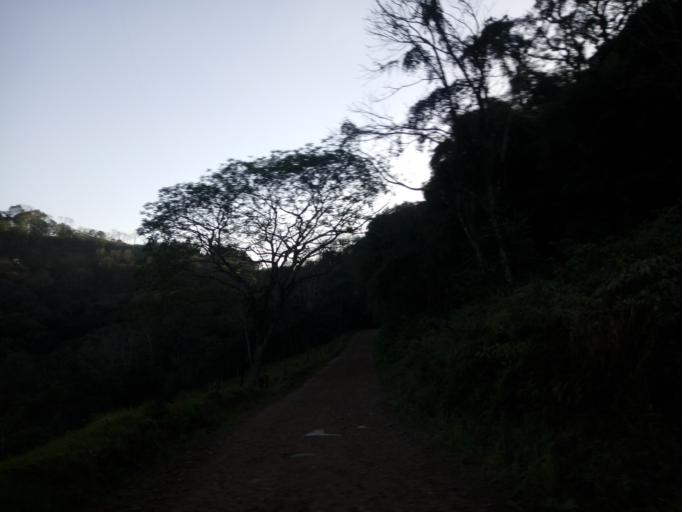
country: BR
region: Santa Catarina
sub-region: Chapeco
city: Chapeco
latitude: -27.2330
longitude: -52.6794
